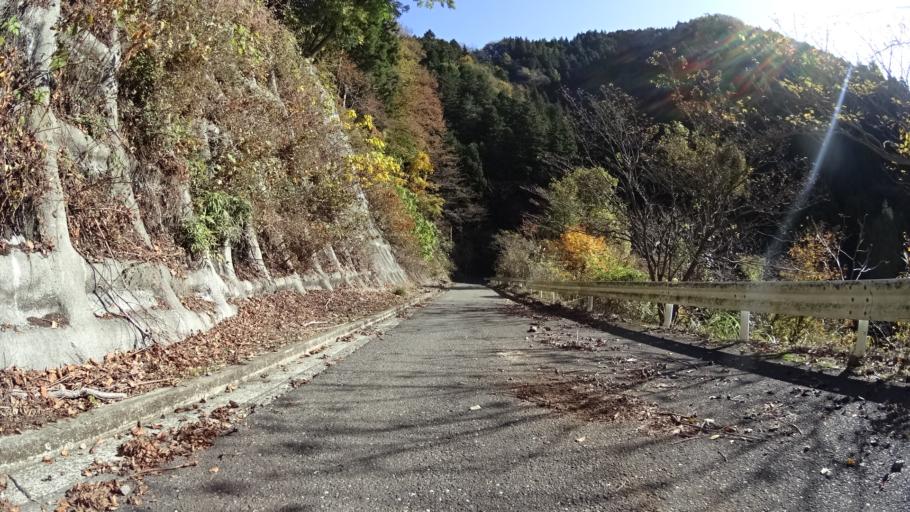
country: JP
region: Kanagawa
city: Atsugi
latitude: 35.5034
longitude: 139.2757
